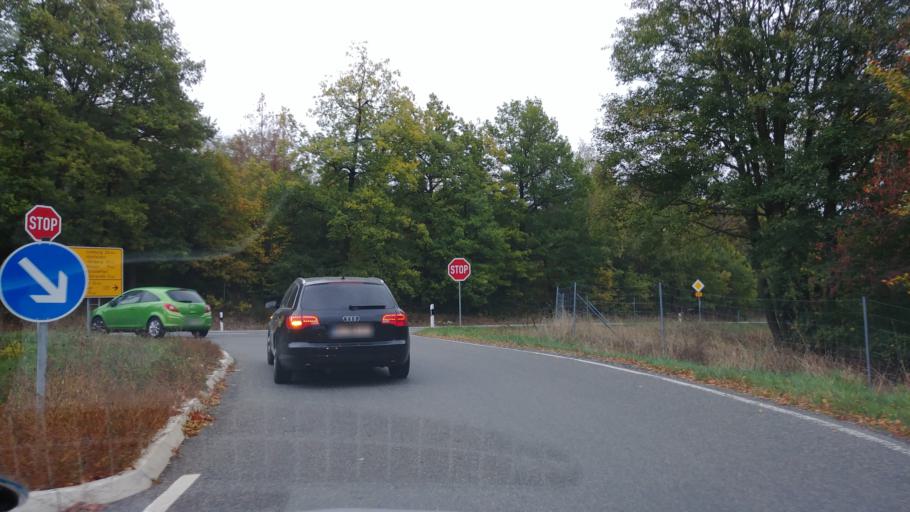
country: DE
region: Hesse
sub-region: Regierungsbezirk Darmstadt
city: Idstein
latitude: 50.2073
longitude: 8.1998
